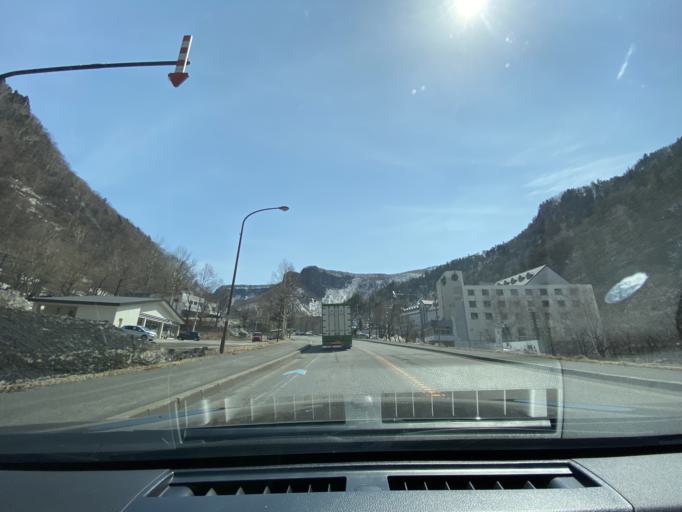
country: JP
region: Hokkaido
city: Kamikawa
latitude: 43.7309
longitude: 142.9422
